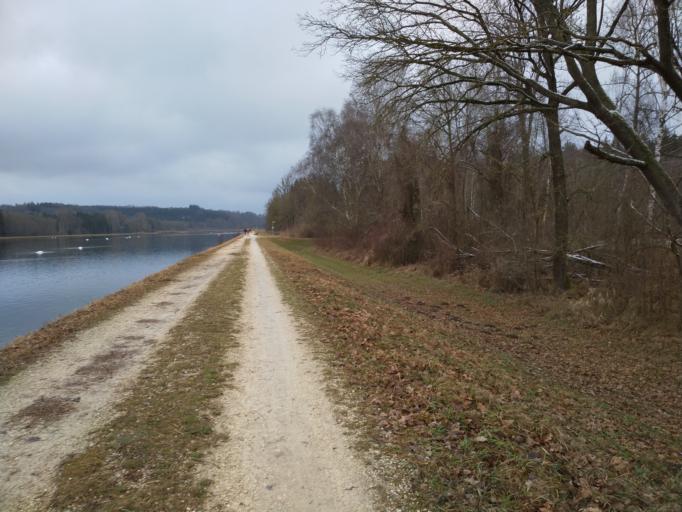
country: DE
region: Bavaria
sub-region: Swabia
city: Rettenbach
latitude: 48.4798
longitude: 10.3257
